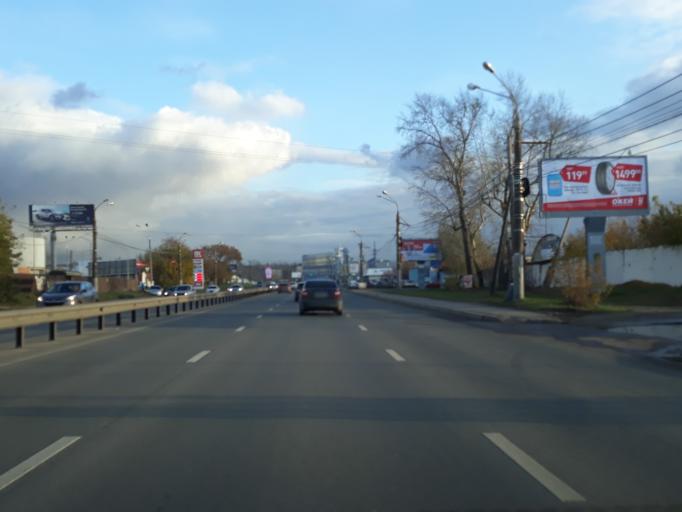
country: RU
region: Nizjnij Novgorod
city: Nizhniy Novgorod
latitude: 56.2995
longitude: 43.9247
